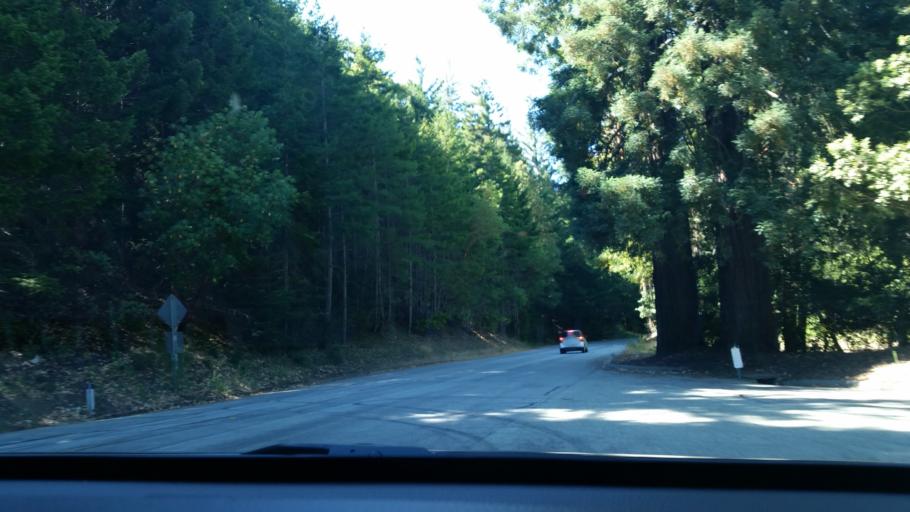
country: US
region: California
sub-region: San Mateo County
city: Woodside
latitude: 37.4301
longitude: -122.2990
